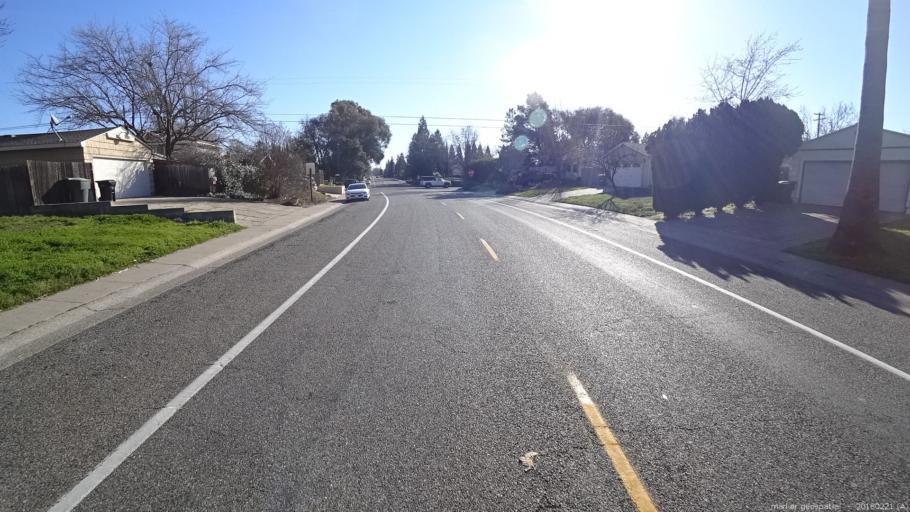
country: US
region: California
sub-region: Sacramento County
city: Orangevale
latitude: 38.6860
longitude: -121.2453
